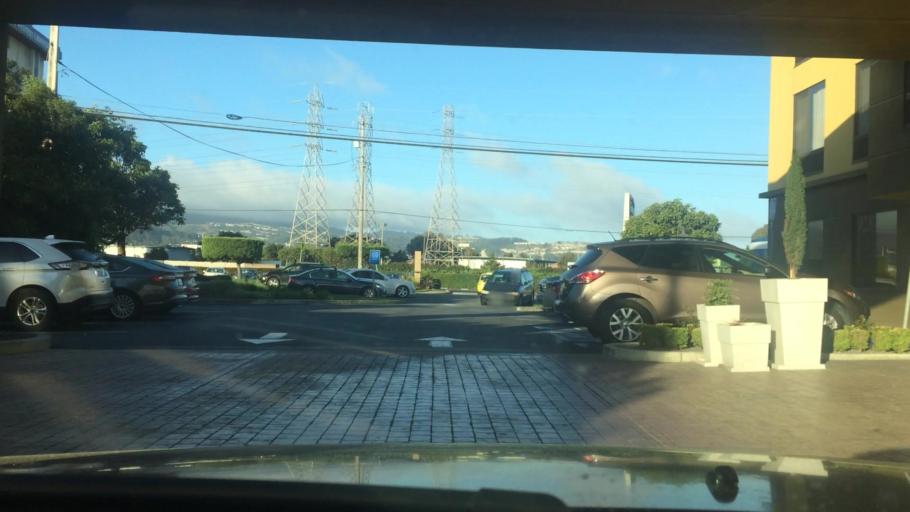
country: US
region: California
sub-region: San Mateo County
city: South San Francisco
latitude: 37.6442
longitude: -122.4038
